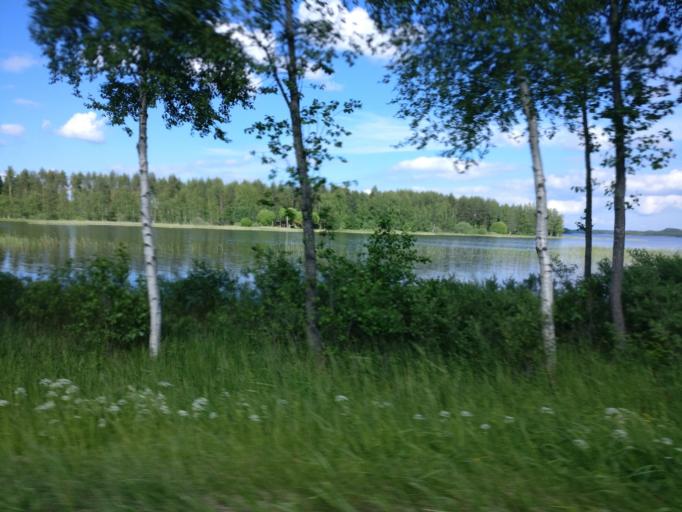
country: FI
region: Southern Savonia
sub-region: Savonlinna
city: Kerimaeki
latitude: 61.8170
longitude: 29.2590
